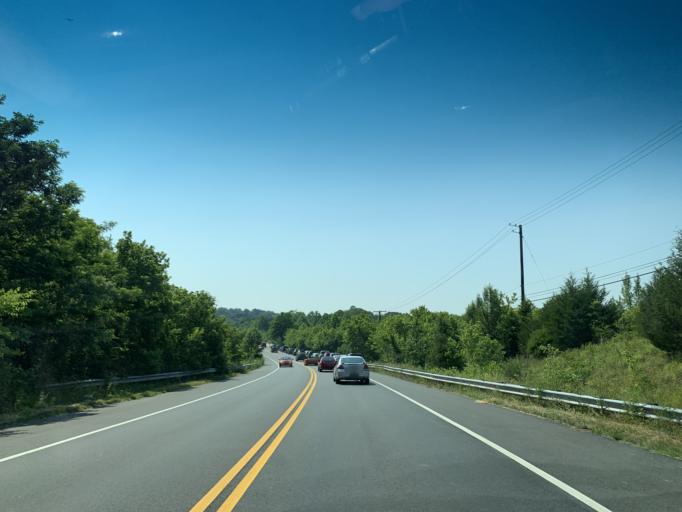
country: US
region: Maryland
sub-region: Montgomery County
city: Darnestown
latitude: 39.1274
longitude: -77.3317
